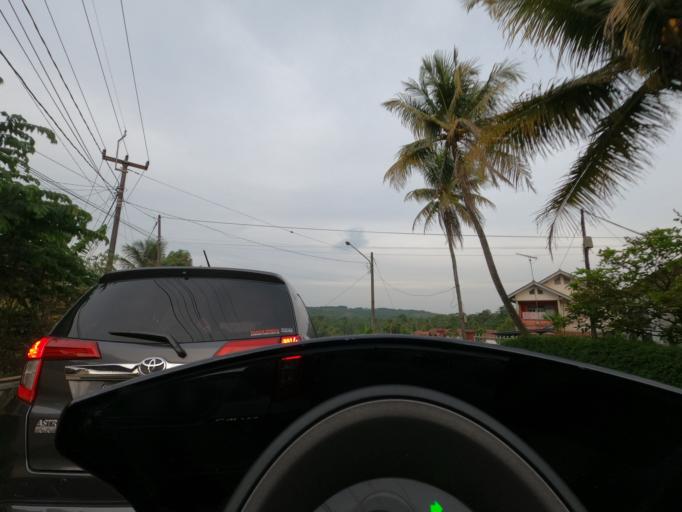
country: ID
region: West Java
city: Lembang
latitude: -6.6606
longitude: 107.7117
